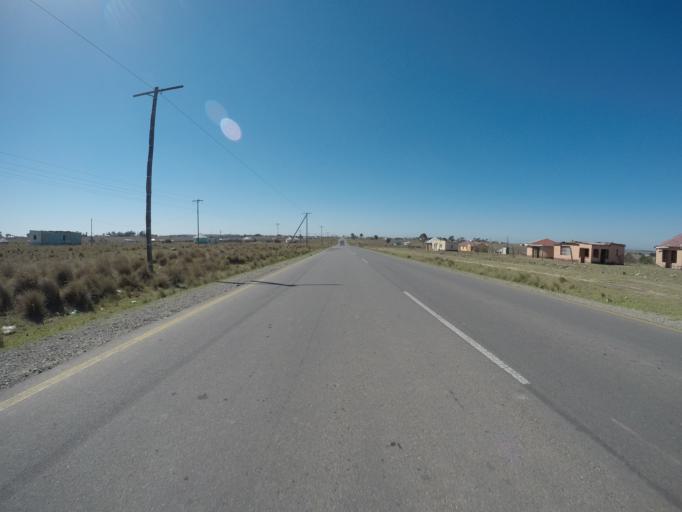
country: ZA
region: Eastern Cape
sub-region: OR Tambo District Municipality
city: Mthatha
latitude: -31.8980
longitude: 28.7879
